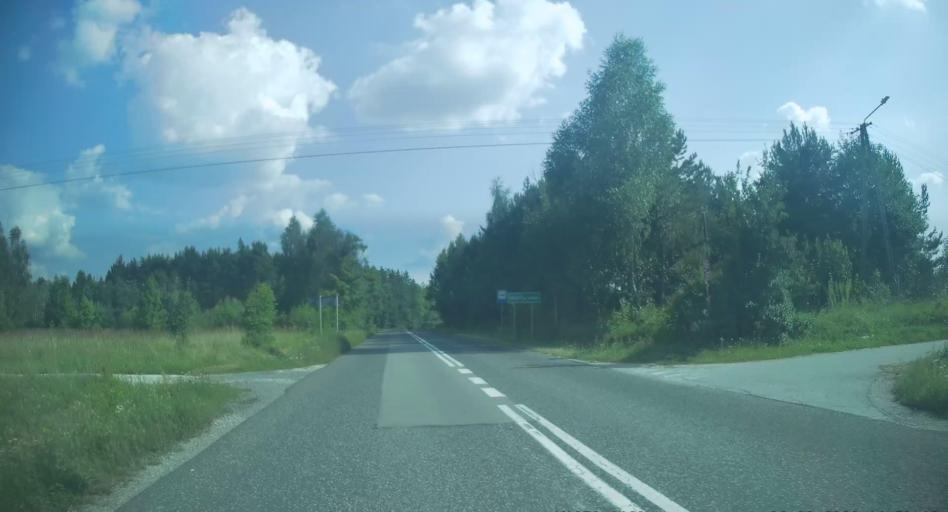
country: PL
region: Swietokrzyskie
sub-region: Powiat kielecki
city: Lopuszno
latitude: 50.8920
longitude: 20.2562
